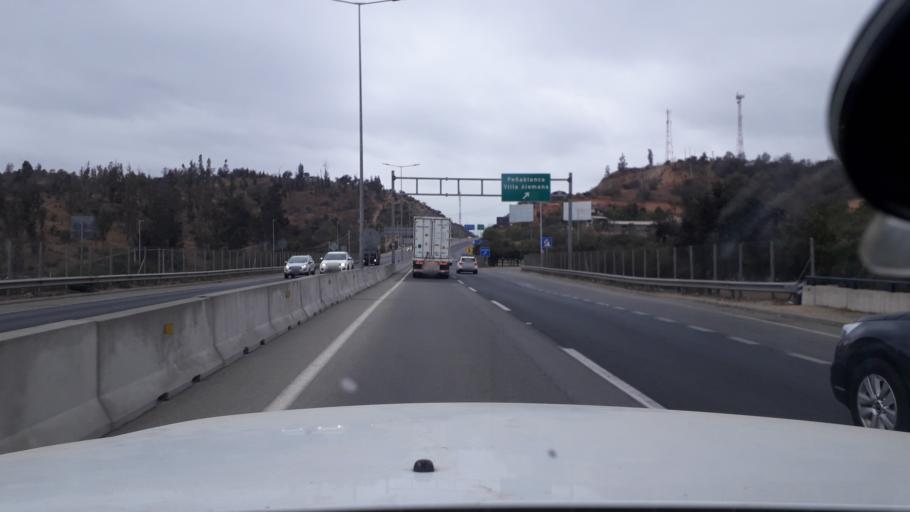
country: CL
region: Valparaiso
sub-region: Provincia de Marga Marga
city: Villa Alemana
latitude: -33.0525
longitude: -71.3330
